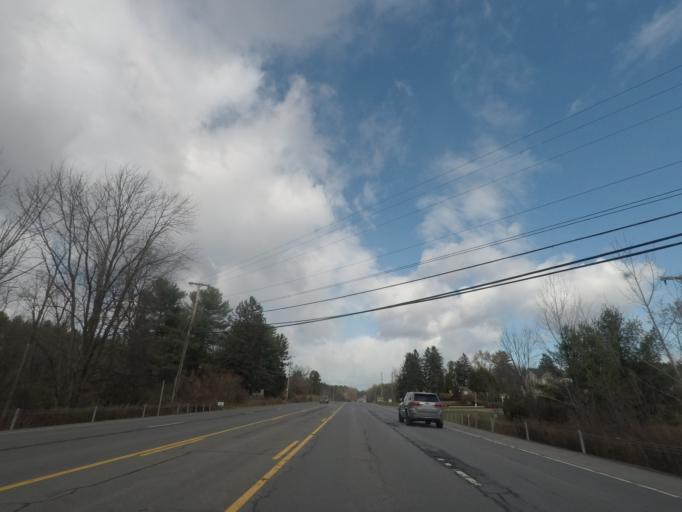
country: US
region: New York
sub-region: Saratoga County
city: Ballston Spa
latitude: 43.0010
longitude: -73.7907
